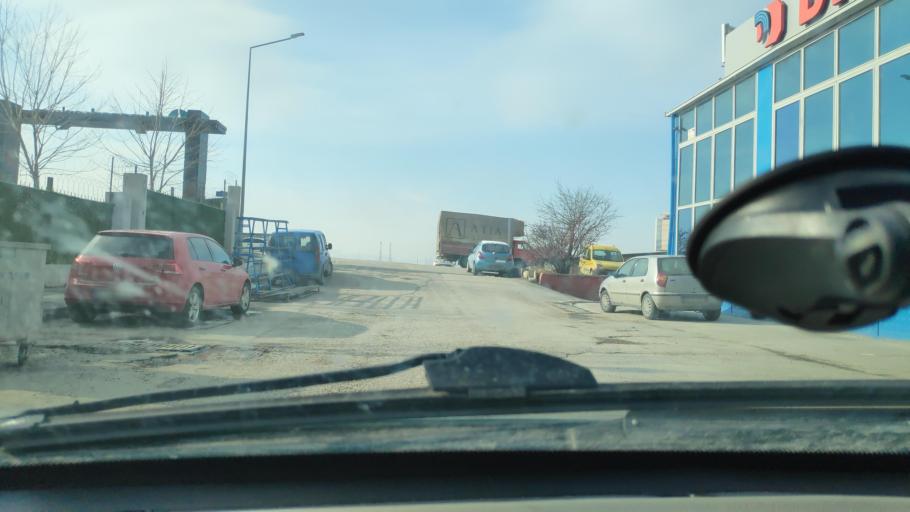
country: TR
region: Ankara
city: Batikent
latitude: 39.9953
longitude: 32.7503
